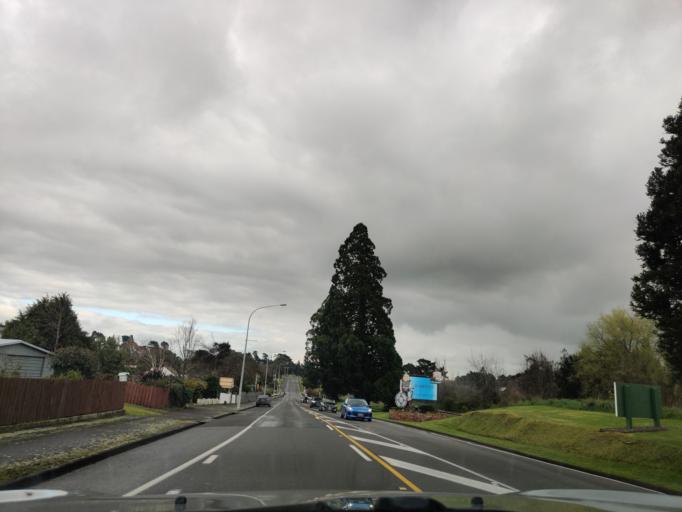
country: NZ
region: Manawatu-Wanganui
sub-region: Palmerston North City
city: Palmerston North
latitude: -40.2126
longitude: 176.0910
